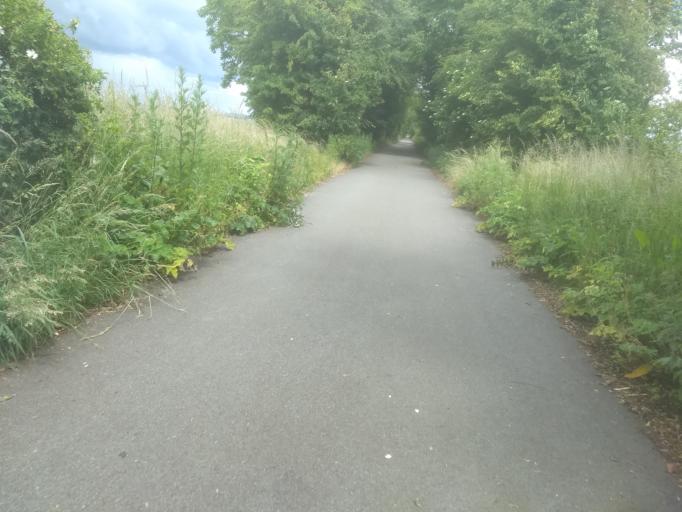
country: FR
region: Nord-Pas-de-Calais
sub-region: Departement du Pas-de-Calais
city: Beaumetz-les-Loges
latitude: 50.2444
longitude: 2.6753
